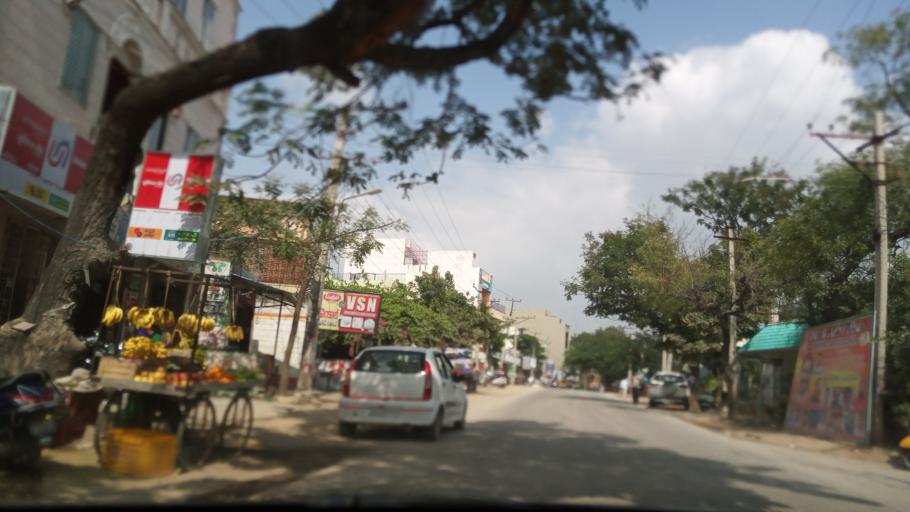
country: IN
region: Andhra Pradesh
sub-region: Chittoor
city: Madanapalle
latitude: 13.5603
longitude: 78.5100
